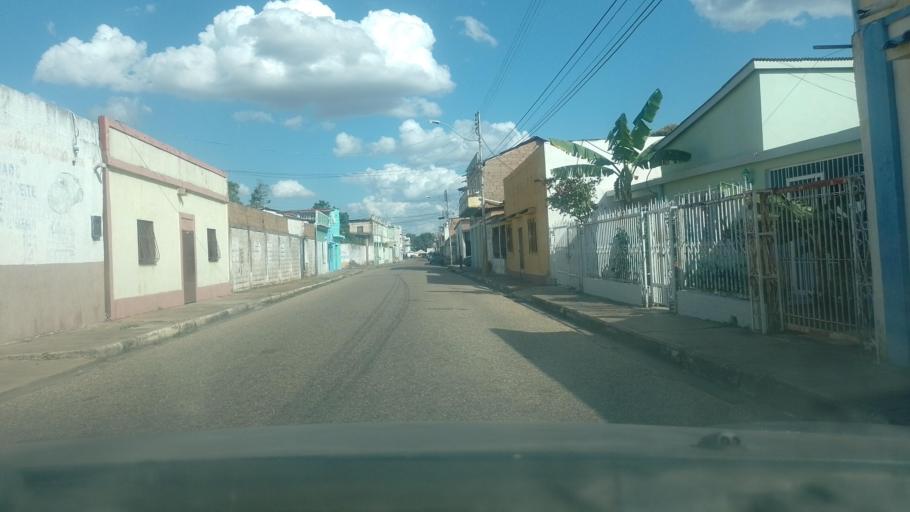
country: VE
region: Anzoategui
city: El Tigre
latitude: 8.8814
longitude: -64.2660
